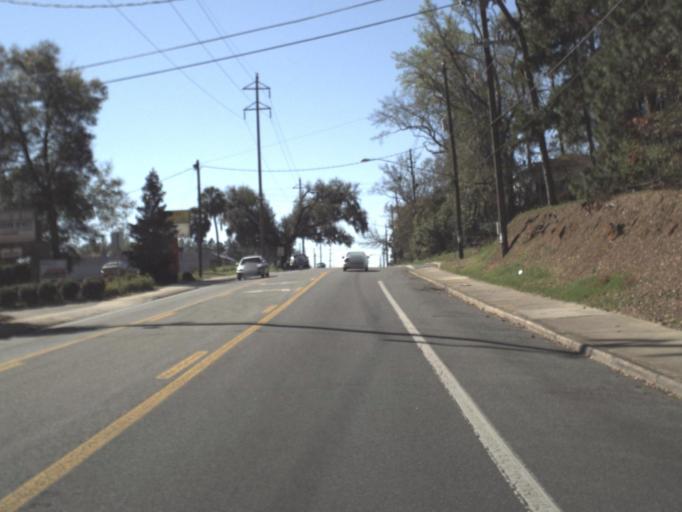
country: US
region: Florida
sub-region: Leon County
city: Tallahassee
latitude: 30.4241
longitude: -84.2820
